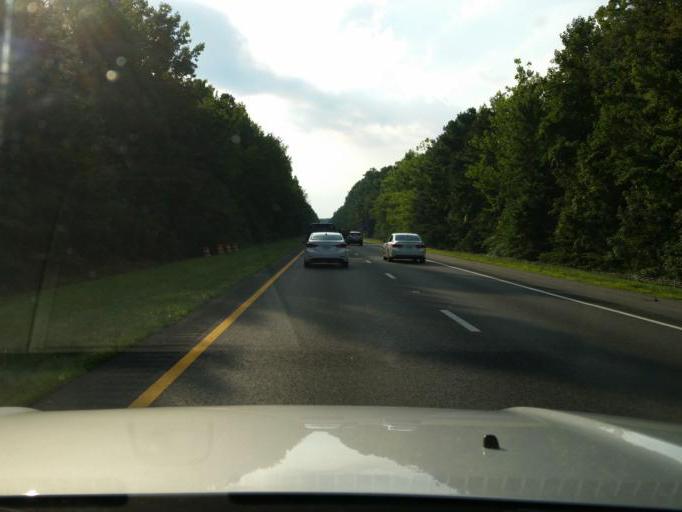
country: US
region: Virginia
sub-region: New Kent County
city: New Kent
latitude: 37.4648
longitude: -76.8900
